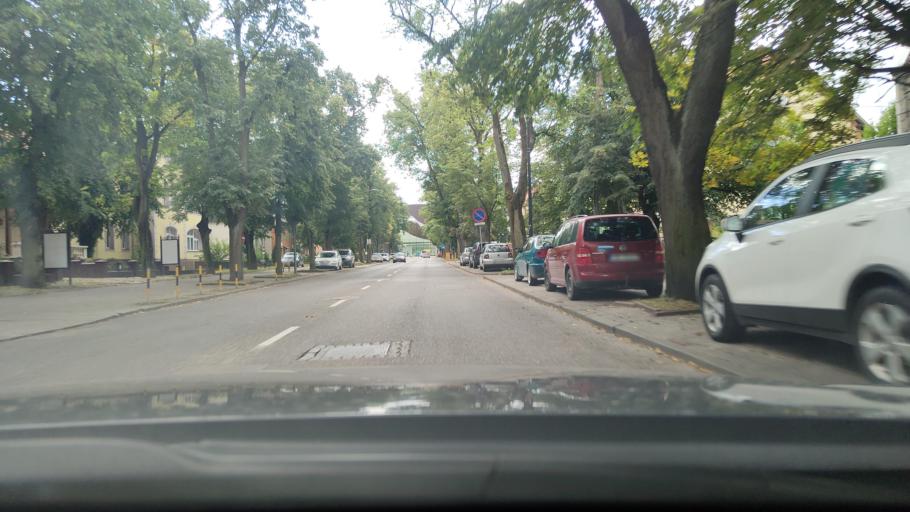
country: PL
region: Pomeranian Voivodeship
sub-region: Powiat wejherowski
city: Wejherowo
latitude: 54.6047
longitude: 18.2287
